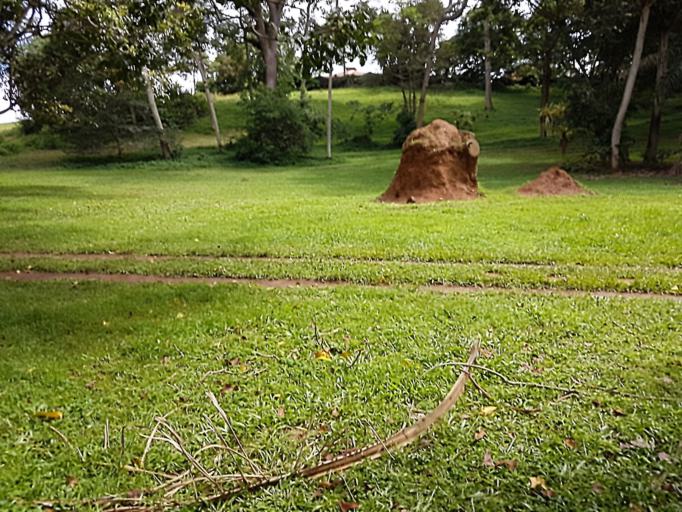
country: UG
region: Central Region
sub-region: Wakiso District
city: Entebbe
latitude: 0.0615
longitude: 32.4780
